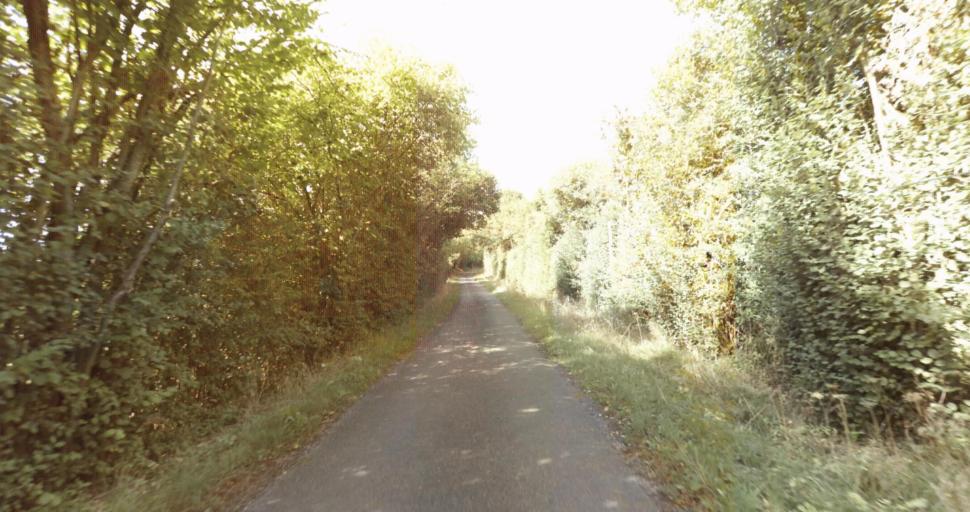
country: FR
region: Lower Normandy
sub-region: Departement de l'Orne
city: Sees
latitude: 48.7093
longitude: 0.1763
